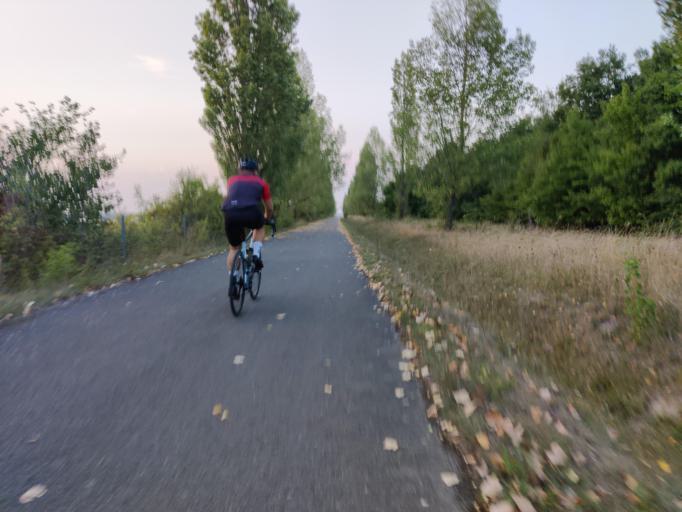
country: DE
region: Saxony
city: Zschortau
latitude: 51.4599
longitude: 12.3181
